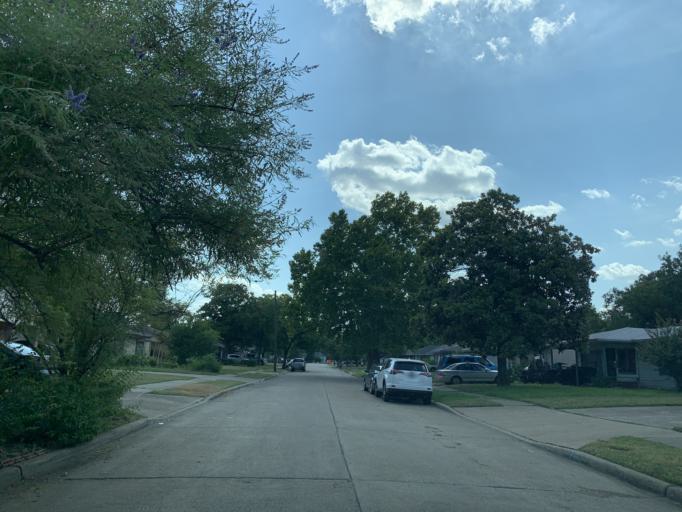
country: US
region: Texas
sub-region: Dallas County
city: Hutchins
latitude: 32.7013
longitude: -96.7740
